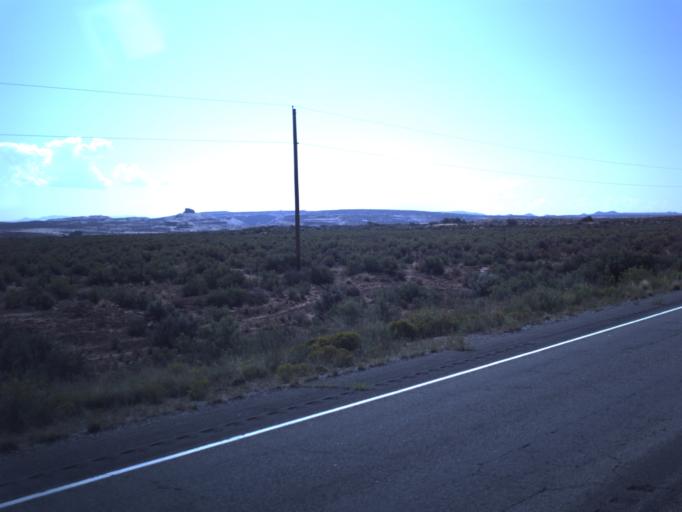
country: US
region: Utah
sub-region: San Juan County
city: Blanding
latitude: 37.1021
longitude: -109.5470
